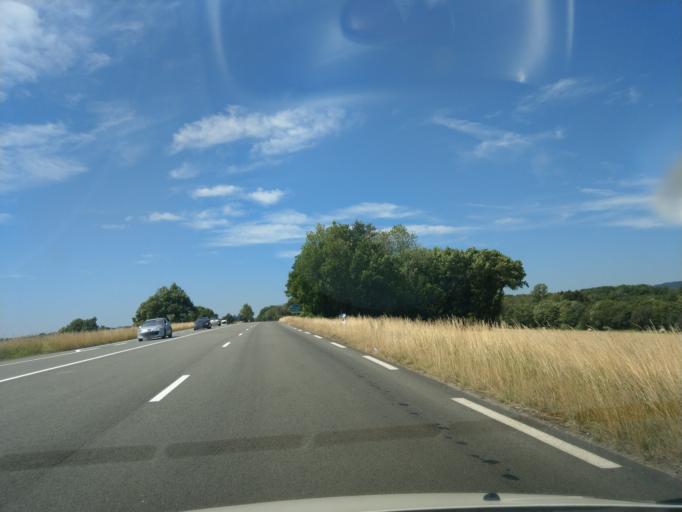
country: FR
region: Franche-Comte
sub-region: Territoire de Belfort
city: Offemont
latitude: 47.6630
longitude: 6.9094
